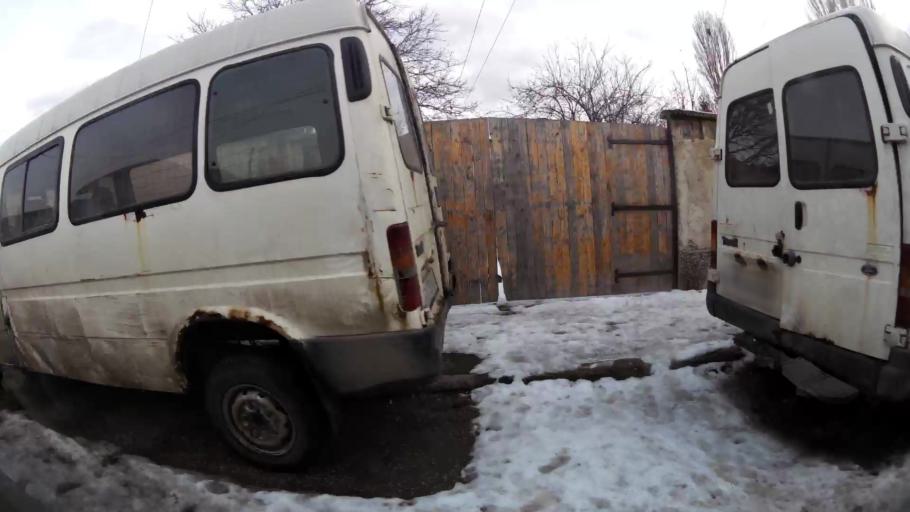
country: BG
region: Sofia-Capital
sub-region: Stolichna Obshtina
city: Sofia
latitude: 42.6879
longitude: 23.3815
